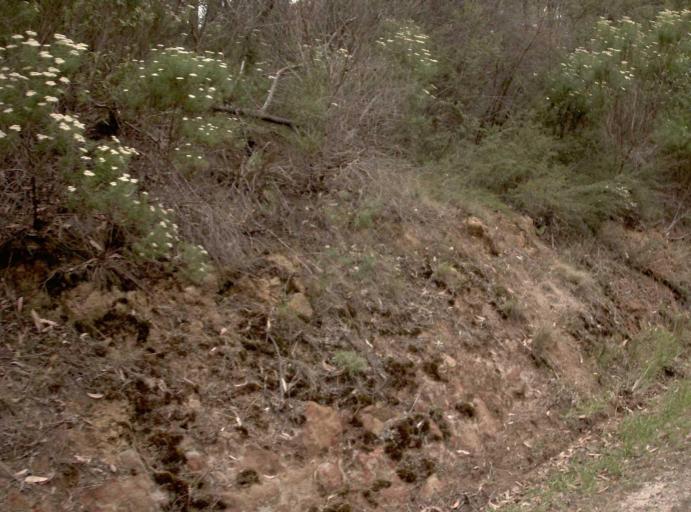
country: AU
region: Victoria
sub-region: Latrobe
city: Traralgon
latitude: -38.4752
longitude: 146.8222
